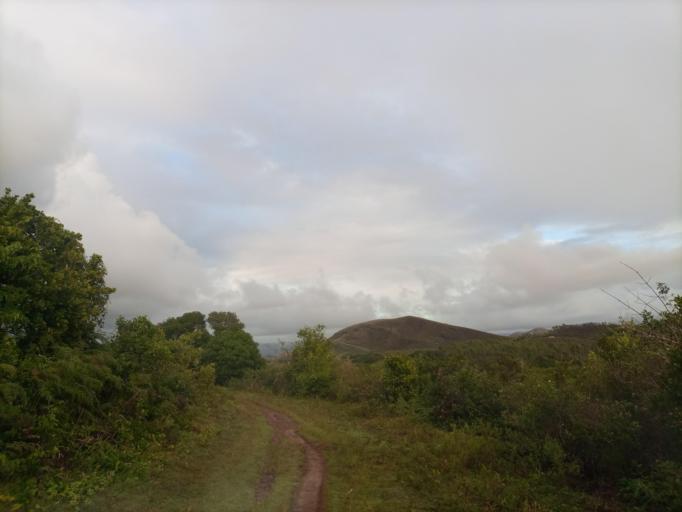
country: MG
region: Anosy
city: Fort Dauphin
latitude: -24.7030
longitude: 47.1780
